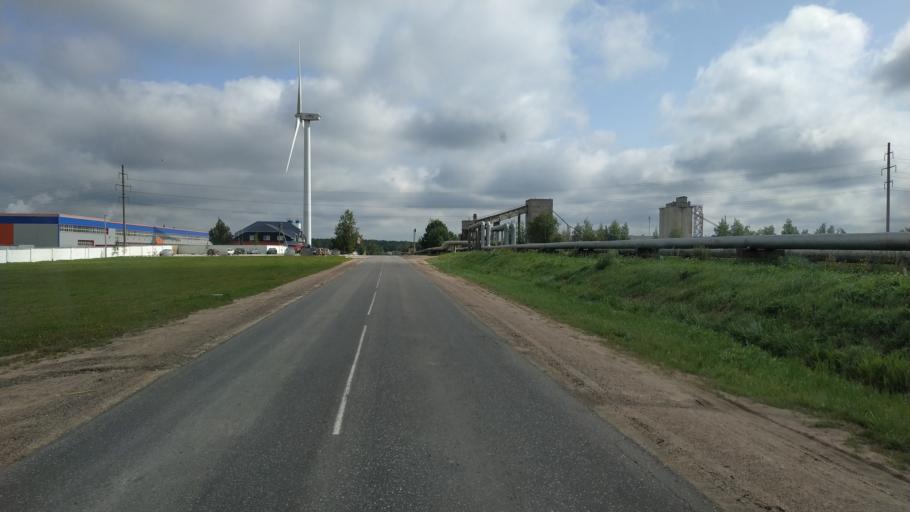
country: BY
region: Mogilev
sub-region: Mahilyowski Rayon
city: Veyno
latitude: 53.8394
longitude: 30.3756
